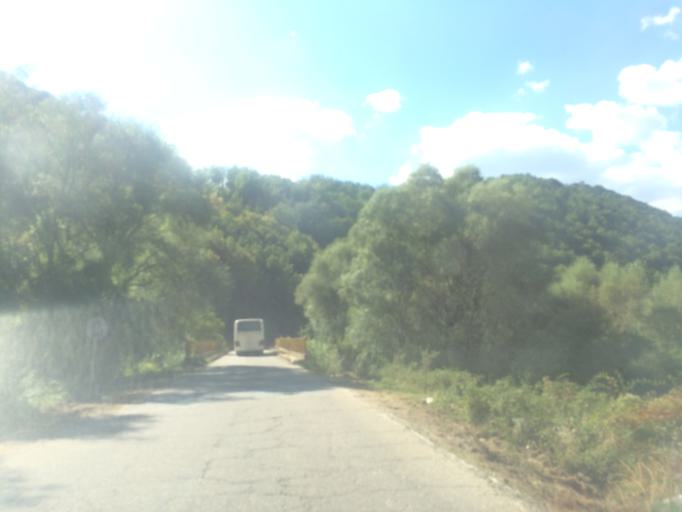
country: MK
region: Makedonska Kamenica
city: Makedonska Kamenica
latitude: 42.0468
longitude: 22.5709
